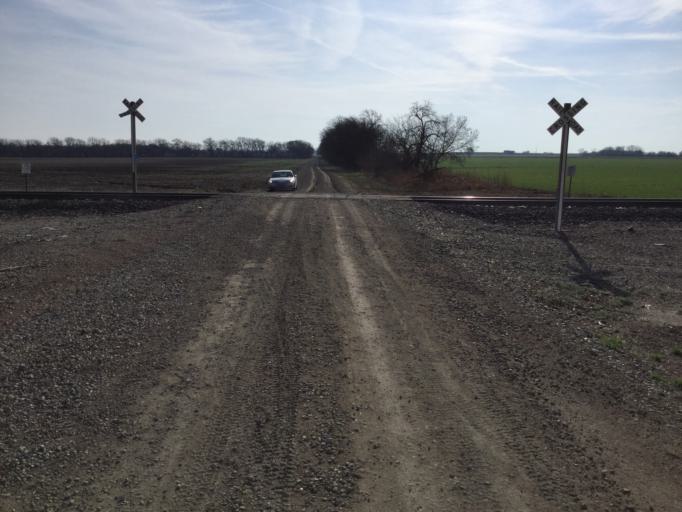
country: US
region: Kansas
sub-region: Butler County
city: Douglass
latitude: 37.5342
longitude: -97.0059
